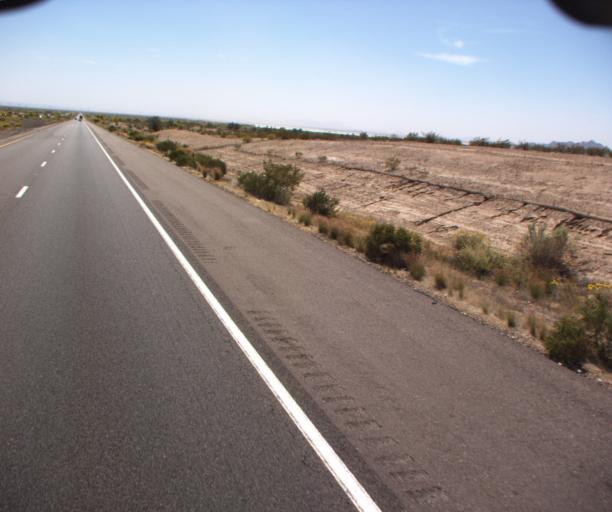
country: US
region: Arizona
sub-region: Maricopa County
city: Gila Bend
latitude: 33.0874
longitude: -112.6482
